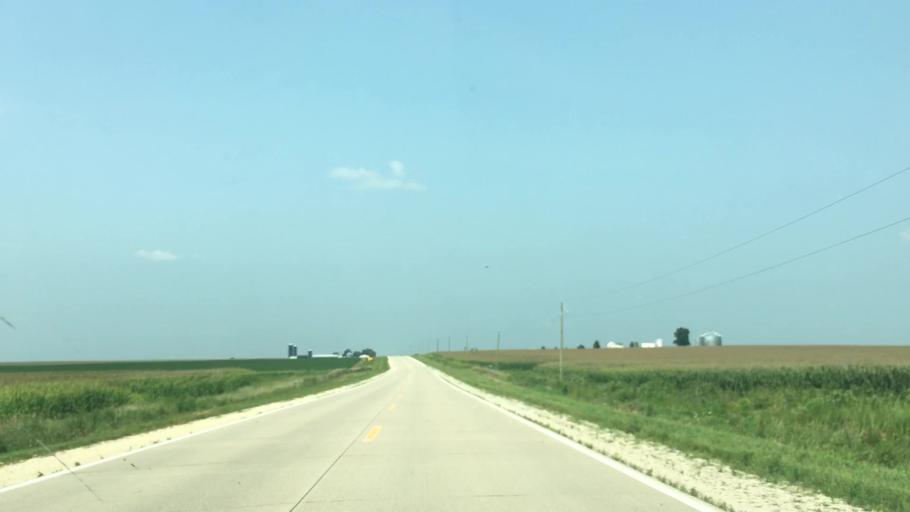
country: US
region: Iowa
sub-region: Fayette County
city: Fayette
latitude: 42.7290
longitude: -91.8041
